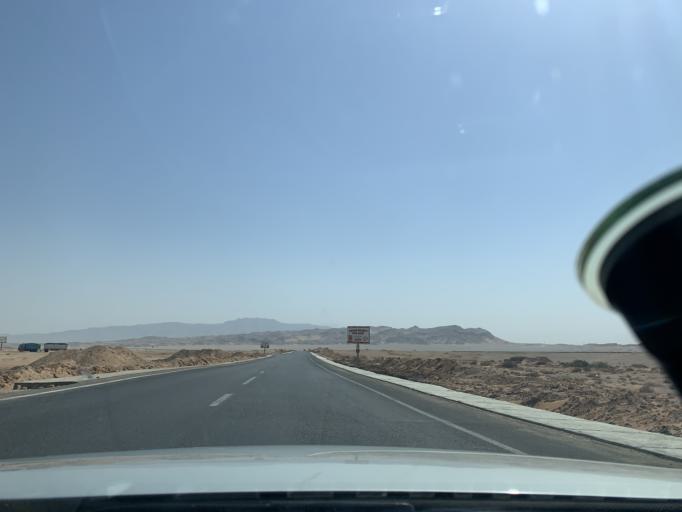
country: EG
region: As Suways
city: Ain Sukhna
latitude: 29.0809
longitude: 32.6297
